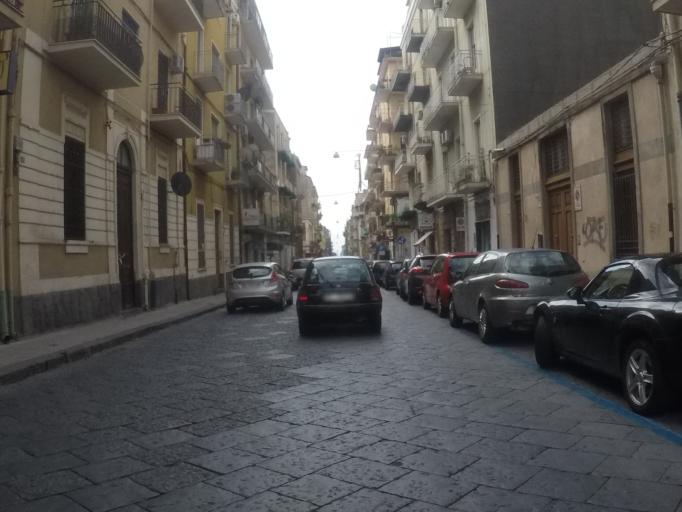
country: IT
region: Sicily
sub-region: Catania
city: Canalicchio
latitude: 37.5214
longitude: 15.0912
